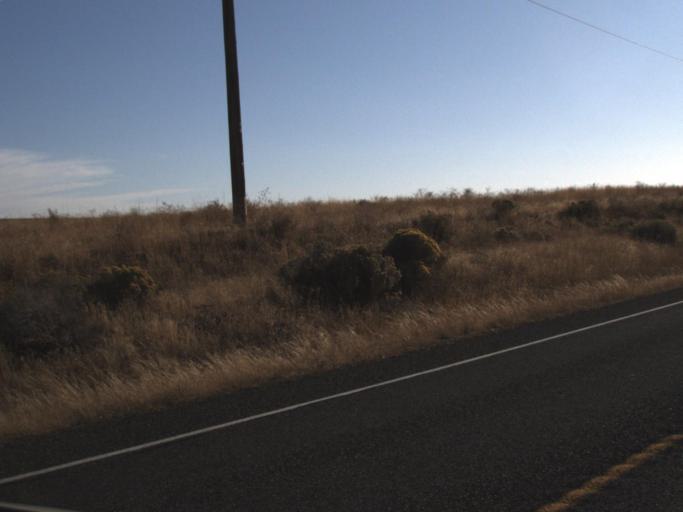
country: US
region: Washington
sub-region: Walla Walla County
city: Burbank
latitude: 46.2871
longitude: -118.7405
